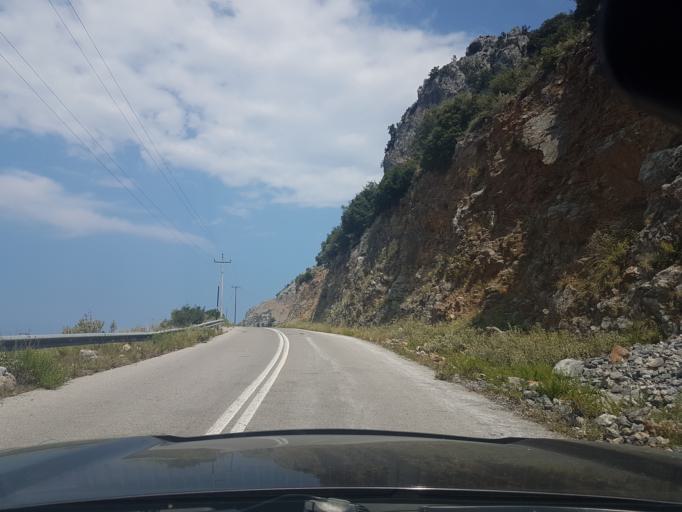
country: GR
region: Central Greece
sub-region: Nomos Evvoias
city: Kymi
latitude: 38.6473
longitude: 23.9627
